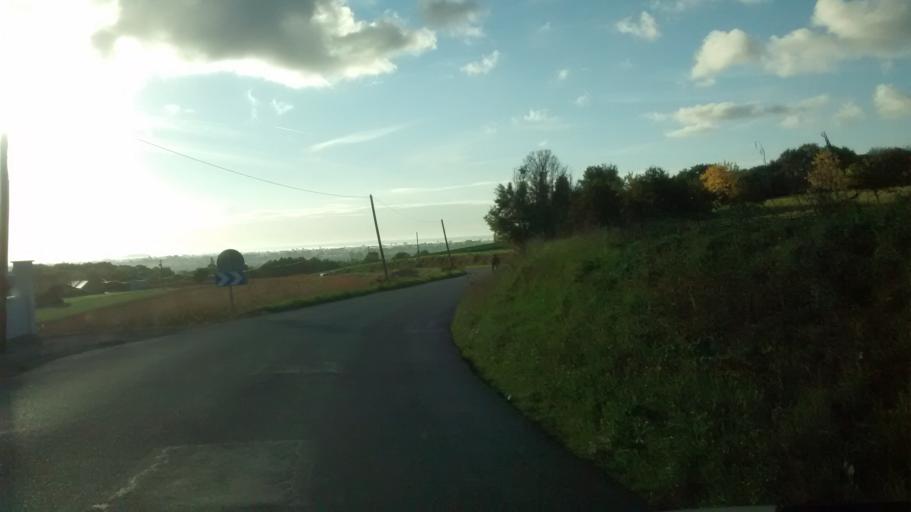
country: FR
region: Brittany
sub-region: Departement d'Ille-et-Vilaine
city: Saint-Meloir-des-Ondes
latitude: 48.6333
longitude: -1.8956
